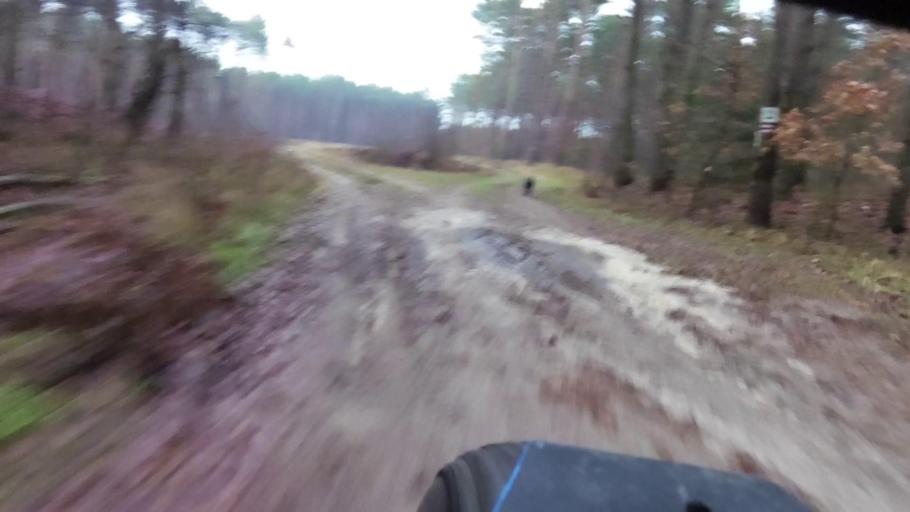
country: PL
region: Lubusz
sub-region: Powiat gorzowski
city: Witnica
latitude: 52.6933
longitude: 14.8136
